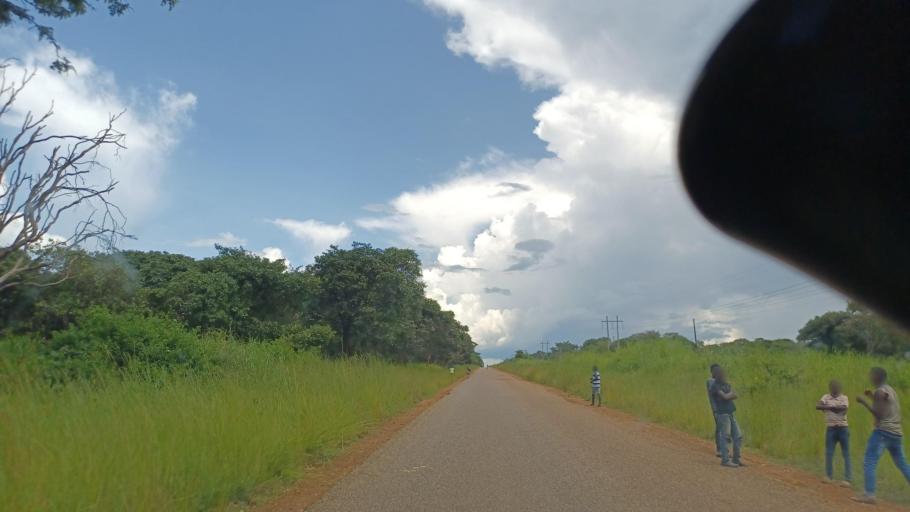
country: ZM
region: North-Western
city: Kasempa
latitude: -12.8686
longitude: 26.0397
